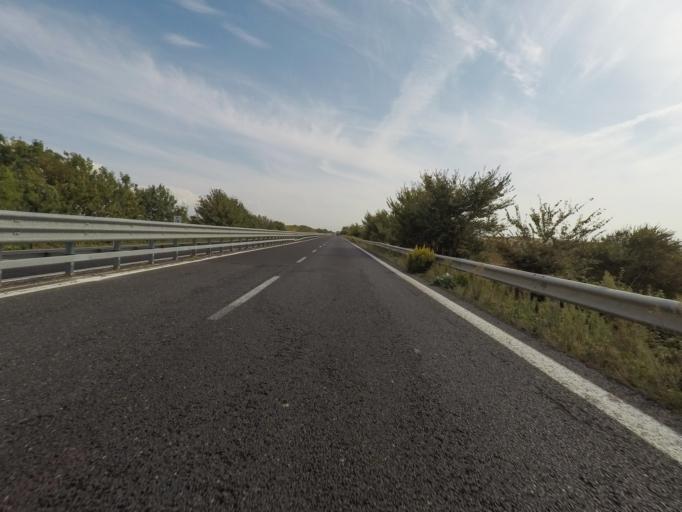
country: IT
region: Latium
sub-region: Provincia di Viterbo
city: Pescia Romana
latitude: 42.3860
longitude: 11.5458
